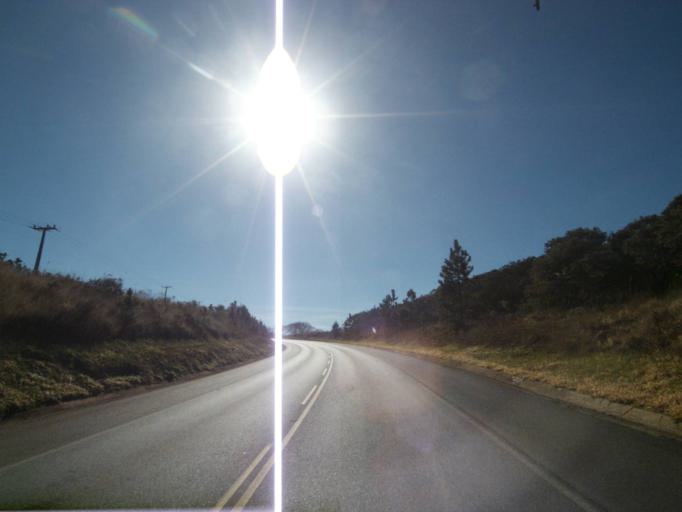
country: BR
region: Parana
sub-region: Tibagi
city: Tibagi
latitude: -24.3981
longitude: -50.3371
